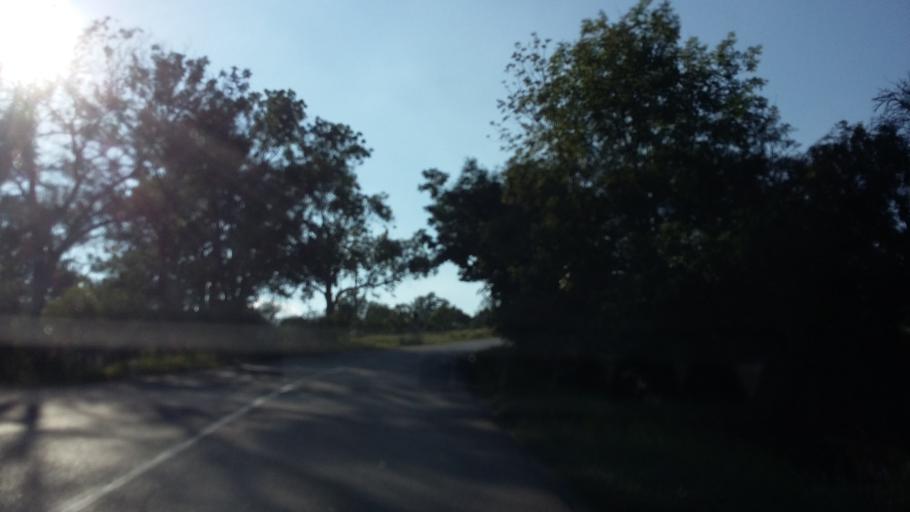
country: CZ
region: South Moravian
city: Ricany
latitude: 49.2153
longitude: 16.3847
